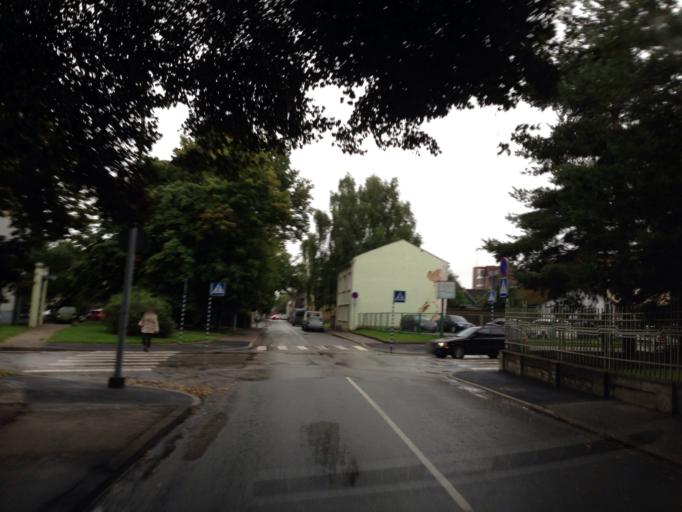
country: EE
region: Tartu
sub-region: Tartu linn
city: Tartu
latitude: 58.3746
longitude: 26.7120
